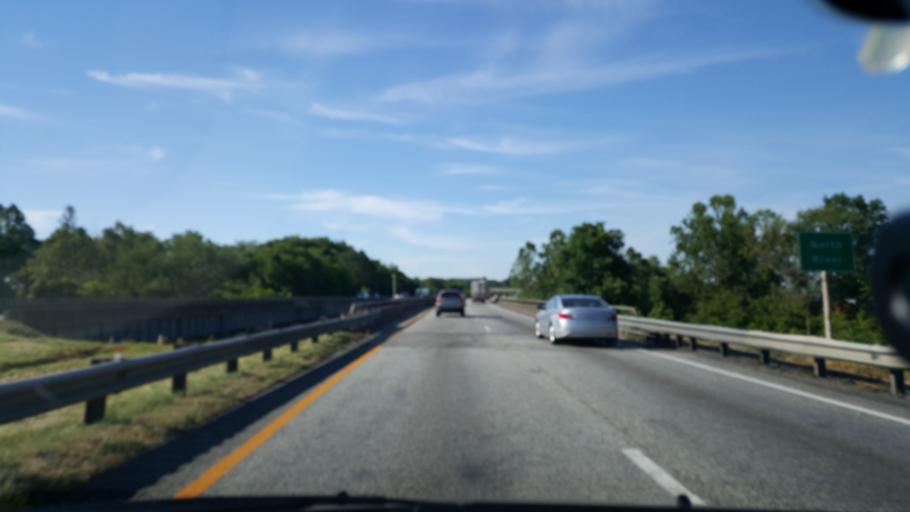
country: US
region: Virginia
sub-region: Rockingham County
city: Bridgewater
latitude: 38.3444
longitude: -78.9337
